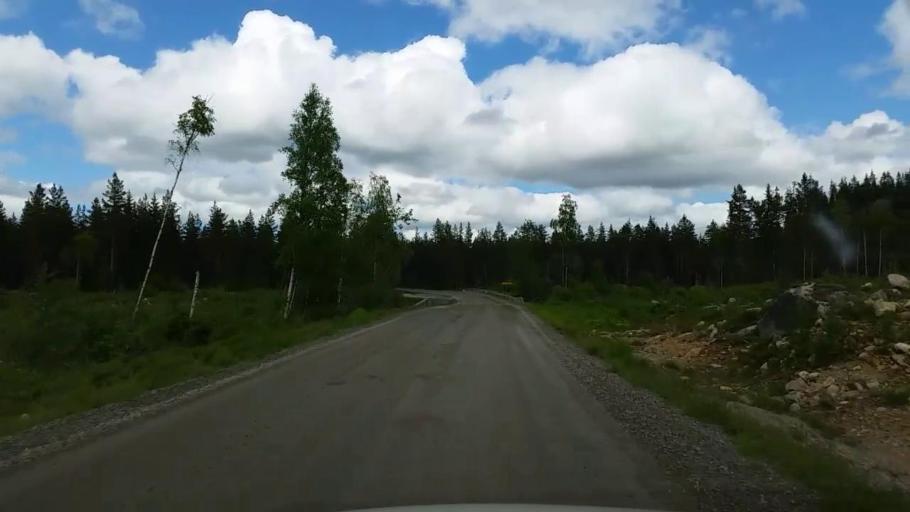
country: SE
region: Gaevleborg
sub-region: Bollnas Kommun
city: Vittsjo
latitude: 61.1530
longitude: 16.1599
